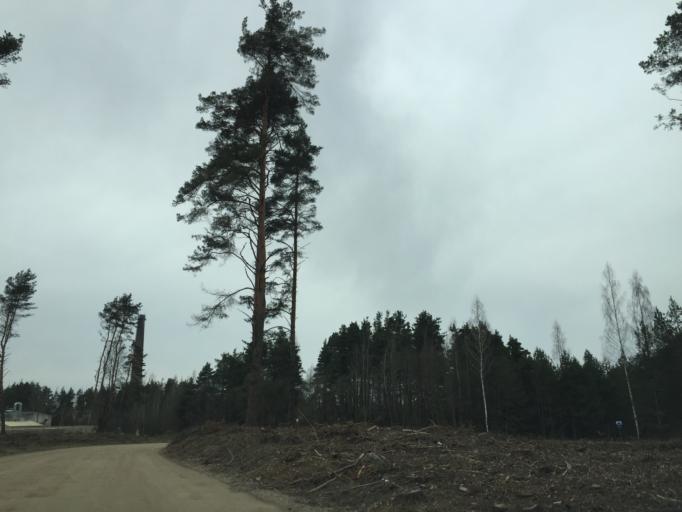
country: LV
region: Jekabpils Rajons
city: Jekabpils
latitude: 56.4873
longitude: 25.8993
